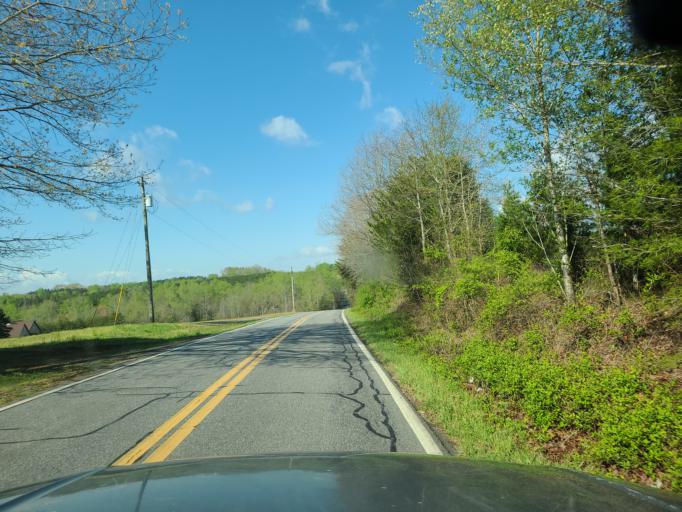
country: US
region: North Carolina
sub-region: Rutherford County
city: Spindale
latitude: 35.3998
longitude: -81.8918
